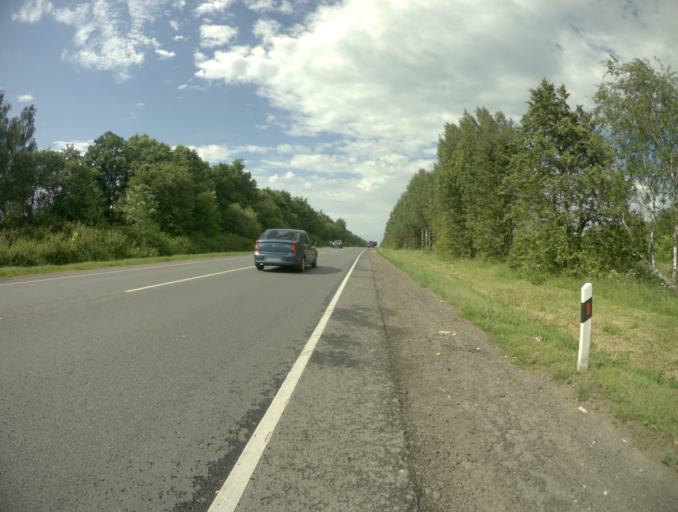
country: RU
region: Vladimir
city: Suzdal'
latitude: 56.3616
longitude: 40.4662
